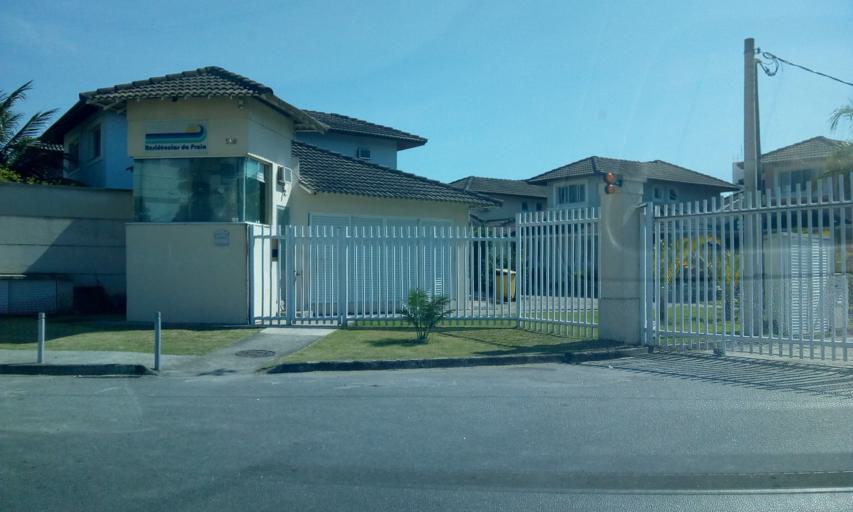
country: BR
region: Rio de Janeiro
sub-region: Nilopolis
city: Nilopolis
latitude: -23.0268
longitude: -43.4771
